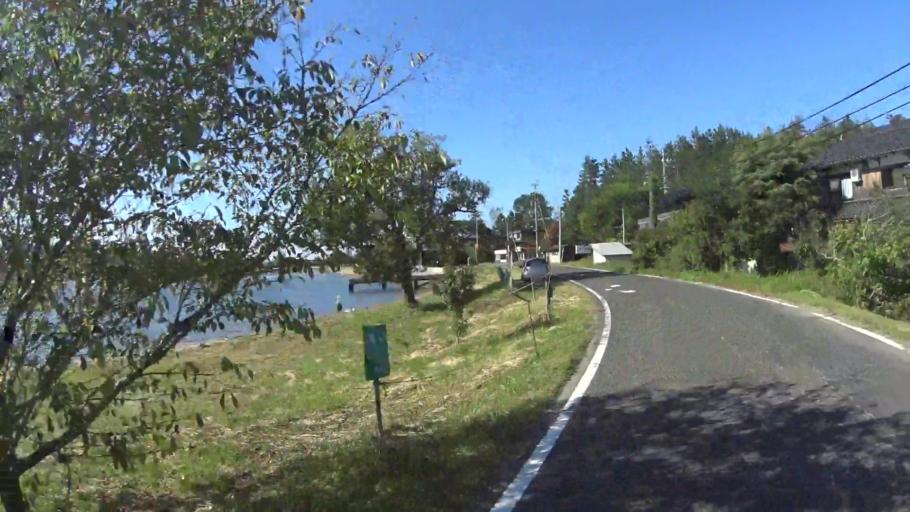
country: JP
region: Hyogo
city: Toyooka
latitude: 35.6386
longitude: 134.9258
